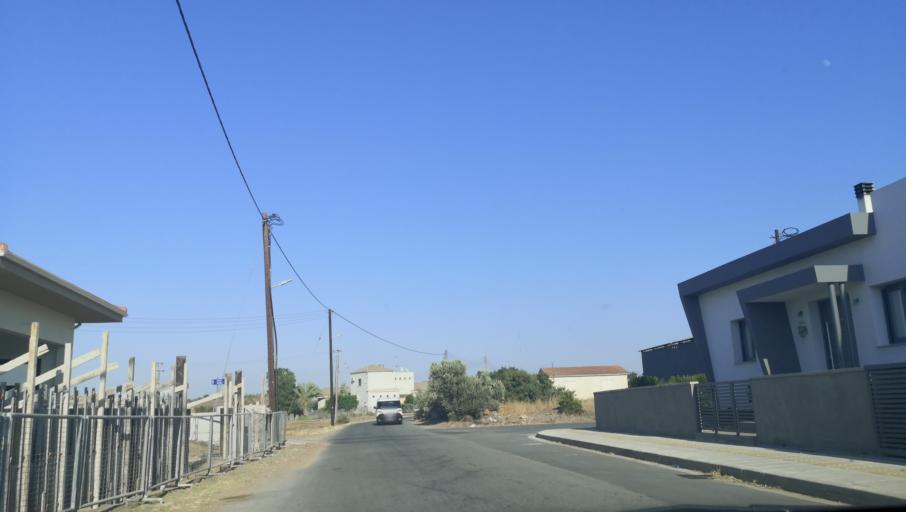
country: CY
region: Lefkosia
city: Psimolofou
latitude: 35.0613
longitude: 33.2724
